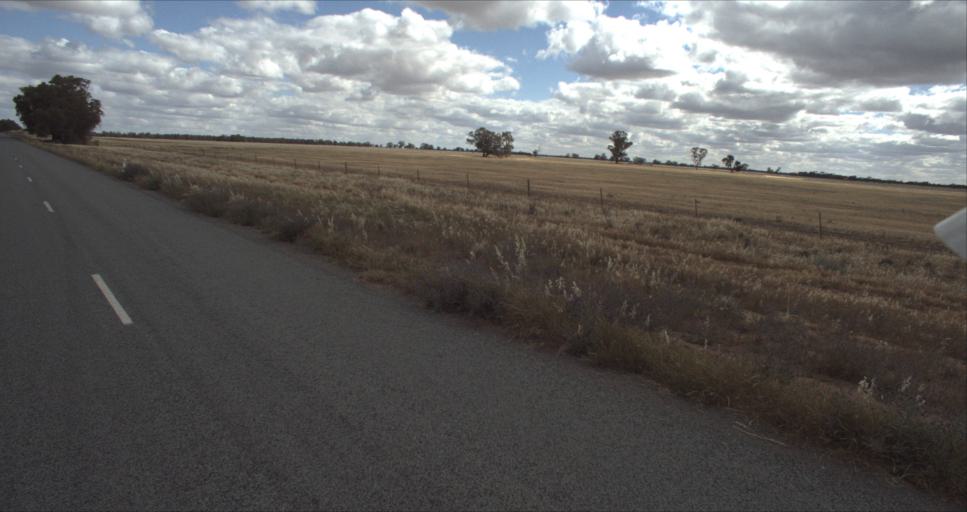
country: AU
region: New South Wales
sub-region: Leeton
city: Leeton
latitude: -34.6696
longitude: 146.3477
